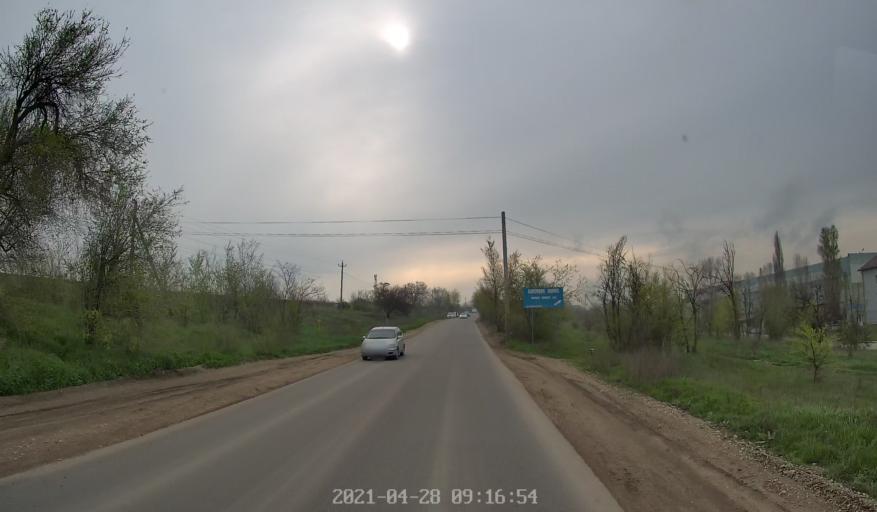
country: MD
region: Chisinau
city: Chisinau
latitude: 46.9883
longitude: 28.9226
